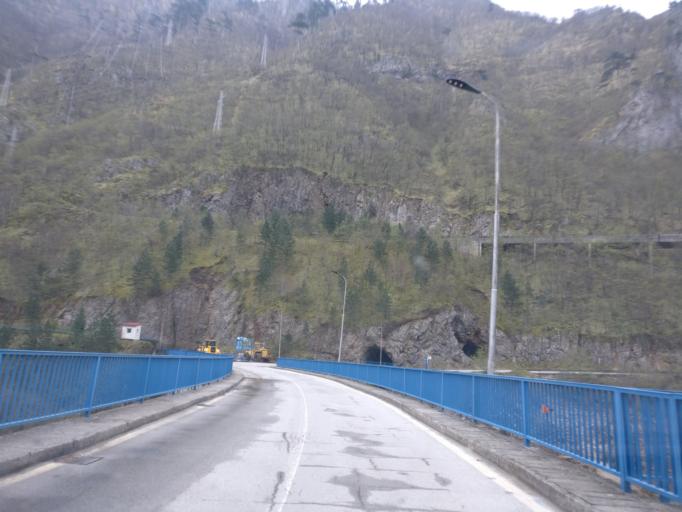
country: ME
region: Opstina Pluzine
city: Pluzine
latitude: 43.2723
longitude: 18.8425
